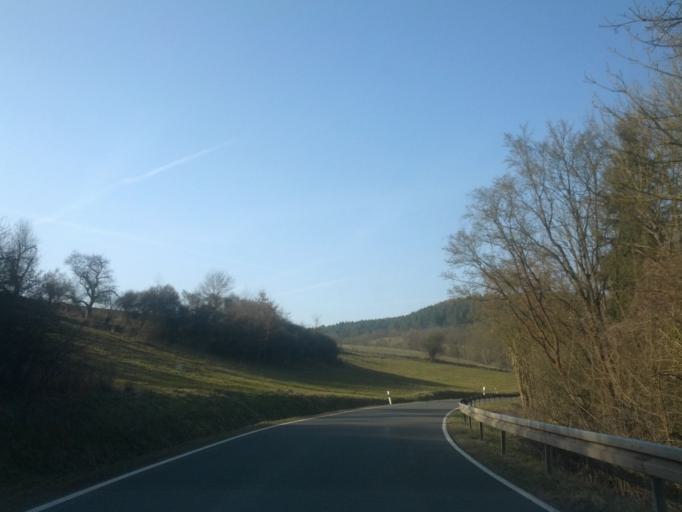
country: DE
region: Thuringia
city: Creuzburg
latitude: 51.0582
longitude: 10.2327
